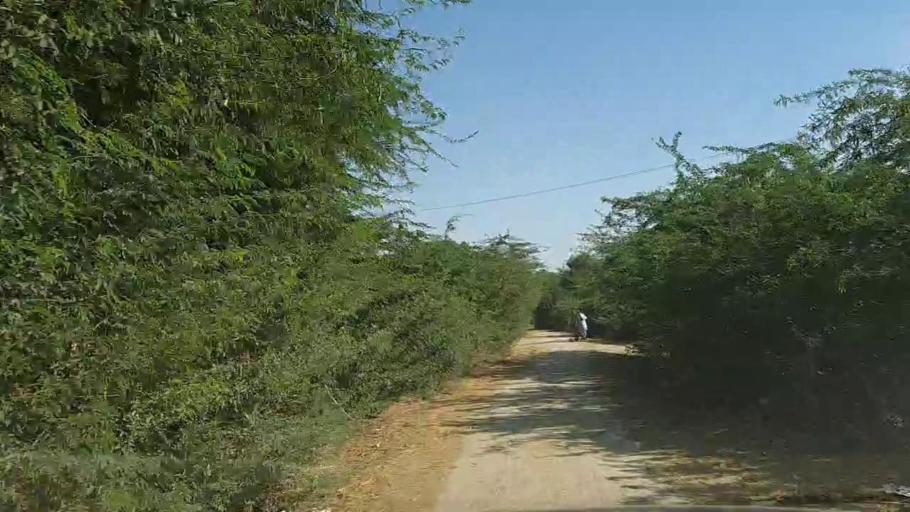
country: PK
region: Sindh
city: Daro Mehar
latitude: 24.7719
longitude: 68.0675
